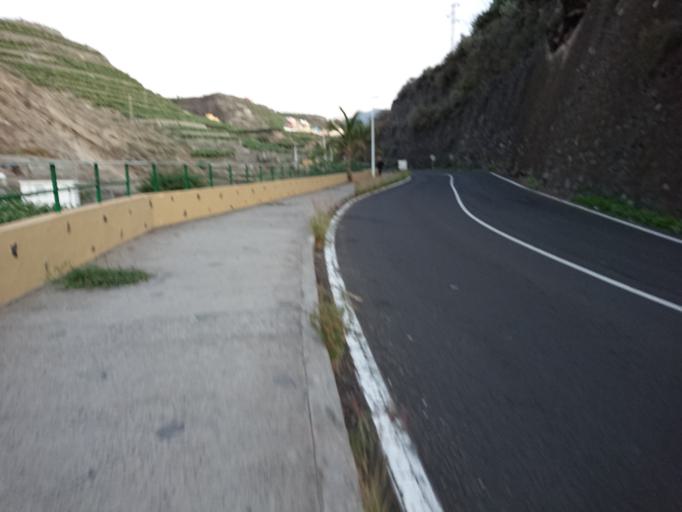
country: ES
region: Canary Islands
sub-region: Provincia de Santa Cruz de Tenerife
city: Tazacorte
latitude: 28.6472
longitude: -17.9400
